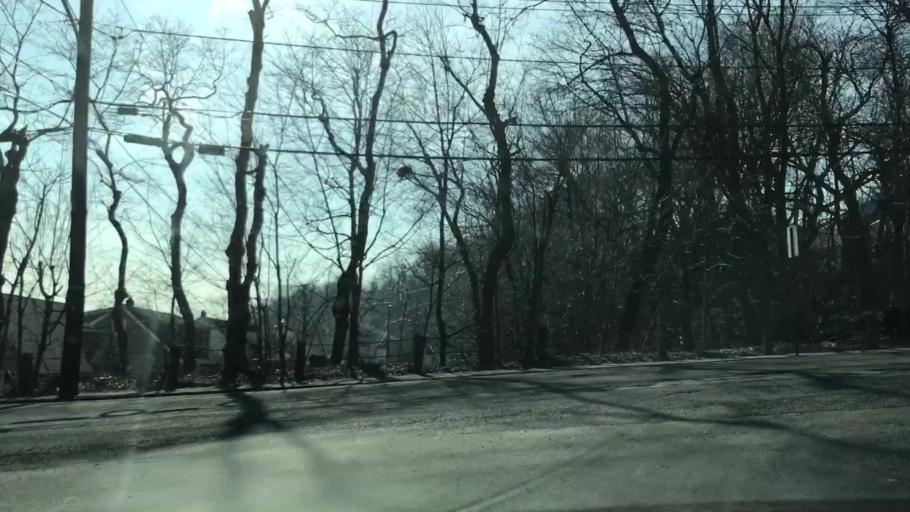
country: US
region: New Jersey
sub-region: Bergen County
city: Hasbrouck Heights
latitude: 40.8554
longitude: -74.0744
